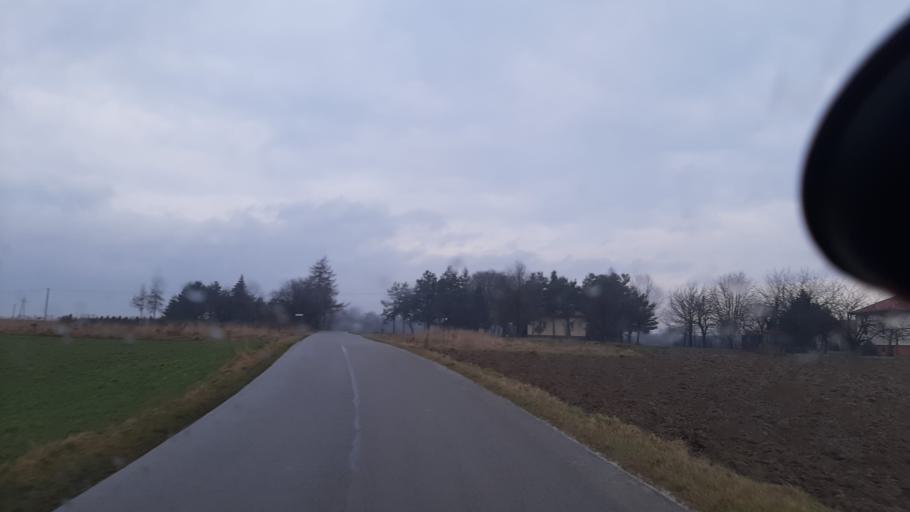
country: PL
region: Lublin Voivodeship
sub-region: Powiat lubelski
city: Niemce
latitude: 51.3342
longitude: 22.5868
